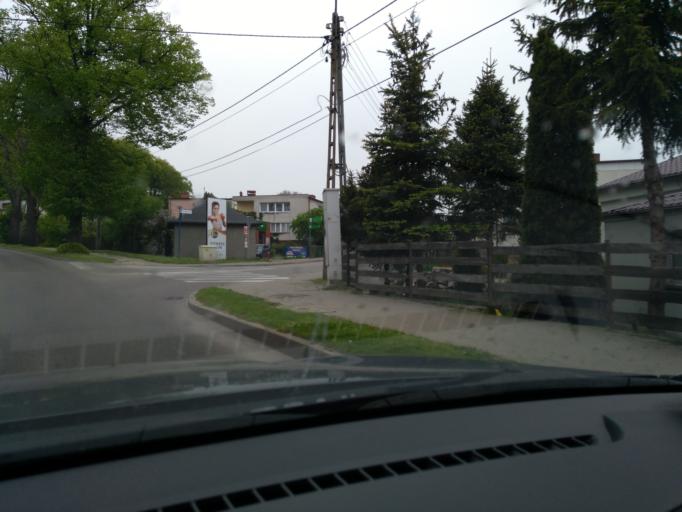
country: PL
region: Pomeranian Voivodeship
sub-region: Powiat kartuski
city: Kartuzy
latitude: 54.3374
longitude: 18.1875
